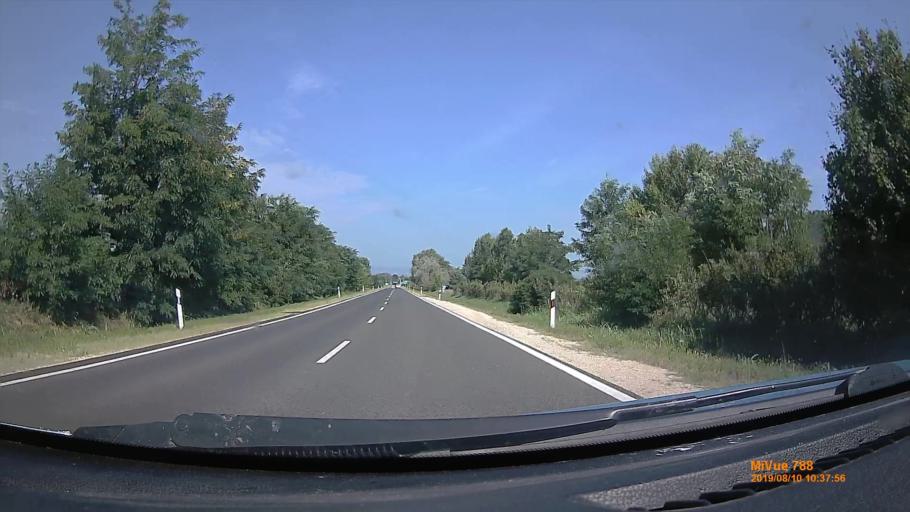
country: HU
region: Somogy
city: Balatonszarszo
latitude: 46.8266
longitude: 17.8526
